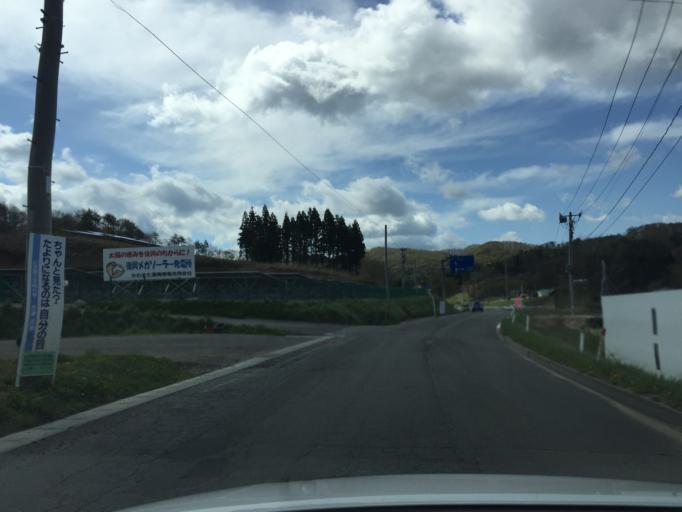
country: JP
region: Fukushima
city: Funehikimachi-funehiki
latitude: 37.6130
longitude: 140.6573
